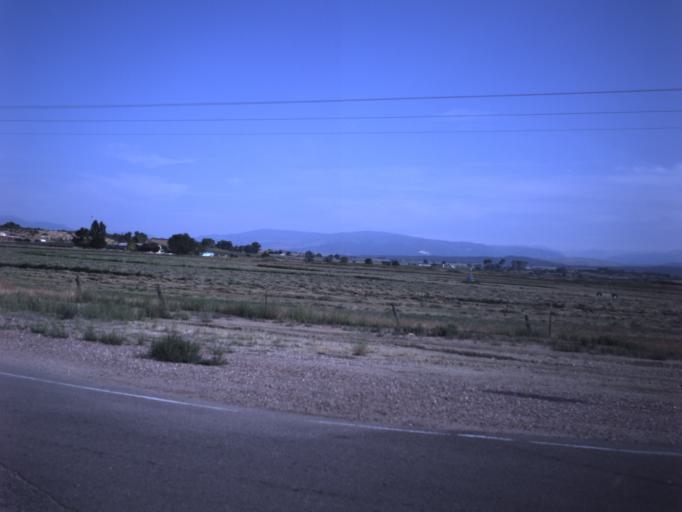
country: US
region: Utah
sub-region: Duchesne County
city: Duchesne
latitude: 40.3592
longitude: -110.2767
